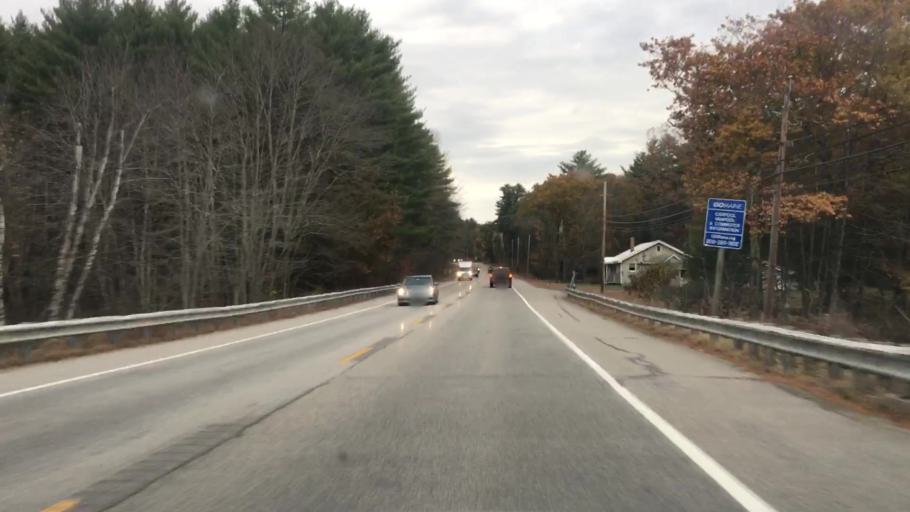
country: US
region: Maine
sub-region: York County
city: Alfred
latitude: 43.4759
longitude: -70.7010
